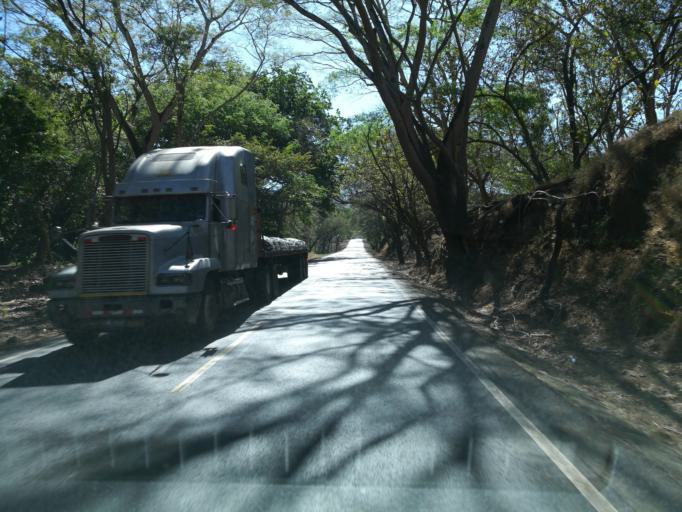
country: CR
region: Puntarenas
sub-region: Canton Central de Puntarenas
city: Puntarenas
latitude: 10.1093
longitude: -84.8863
